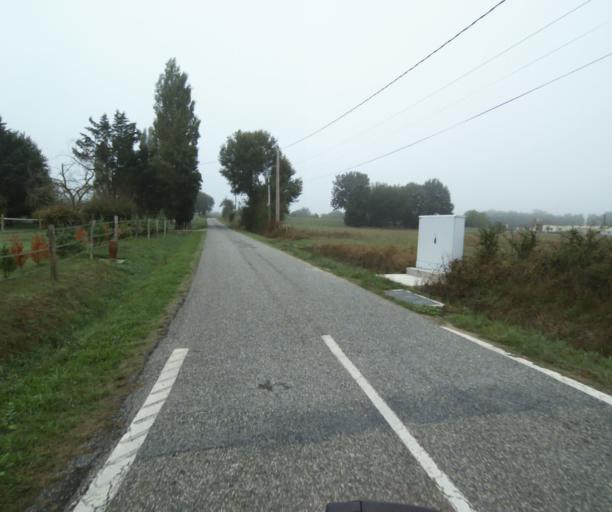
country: FR
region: Midi-Pyrenees
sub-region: Departement du Tarn-et-Garonne
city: Saint-Nauphary
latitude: 43.9497
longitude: 1.4504
